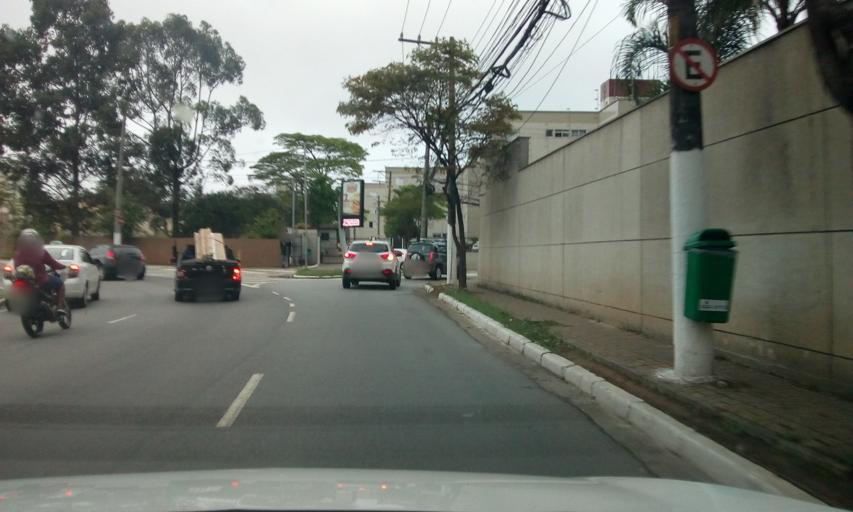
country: BR
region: Sao Paulo
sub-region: Taboao Da Serra
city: Taboao da Serra
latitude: -23.6508
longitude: -46.7189
